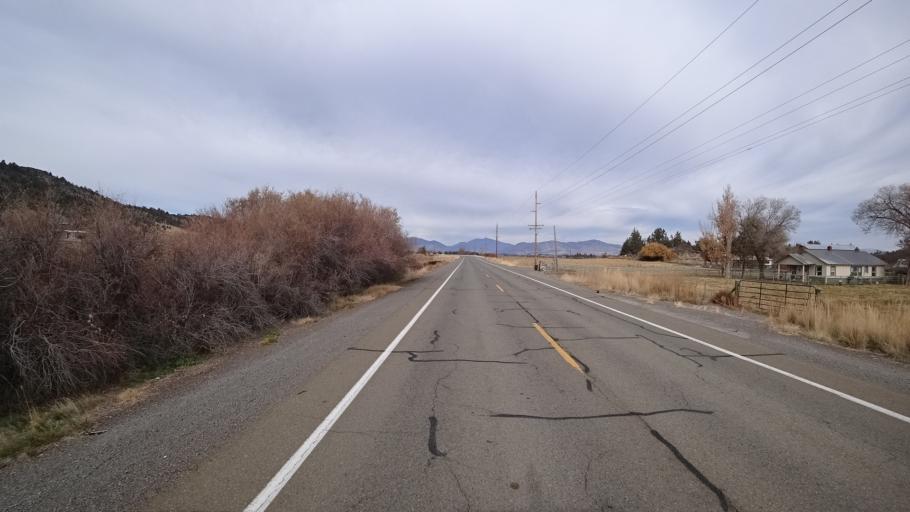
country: US
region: California
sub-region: Siskiyou County
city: Montague
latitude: 41.6771
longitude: -122.5270
